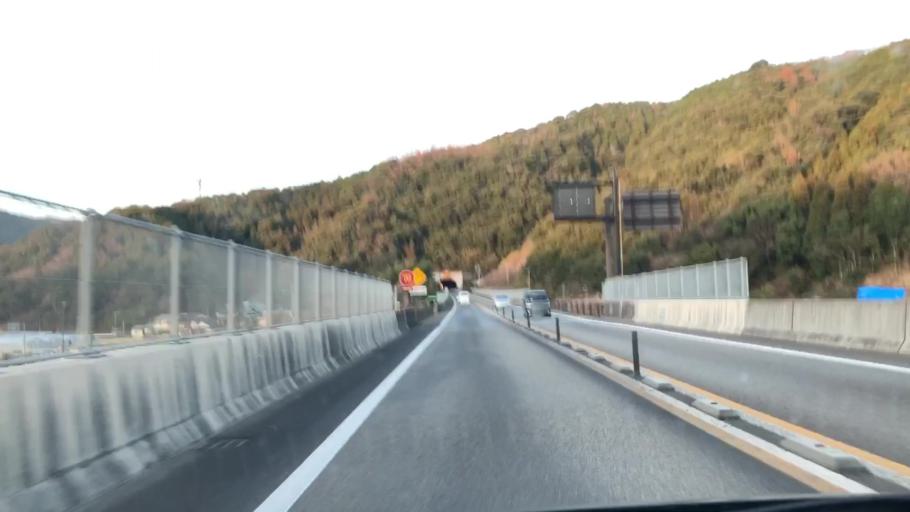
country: JP
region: Kumamoto
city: Minamata
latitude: 32.3004
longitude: 130.5100
